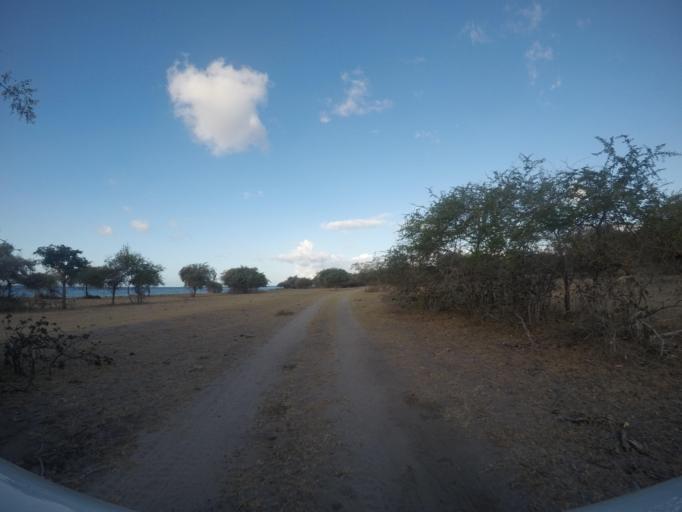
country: TL
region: Lautem
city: Lospalos
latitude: -8.3246
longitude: 126.9897
